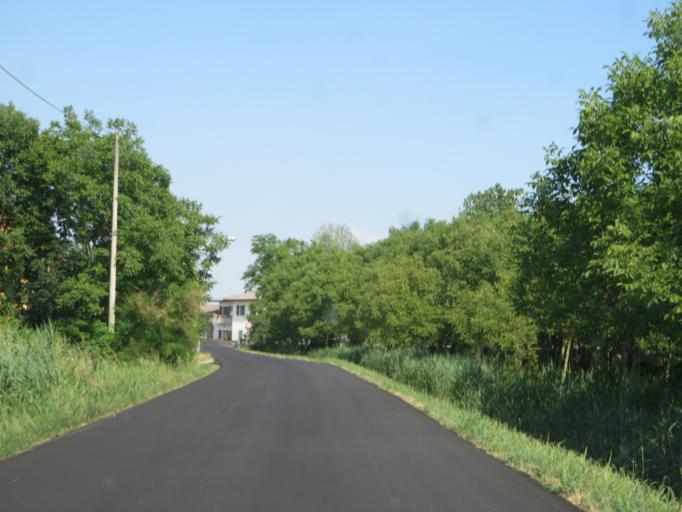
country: IT
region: Veneto
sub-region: Provincia di Verona
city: Angiari
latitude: 45.2231
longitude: 11.2726
